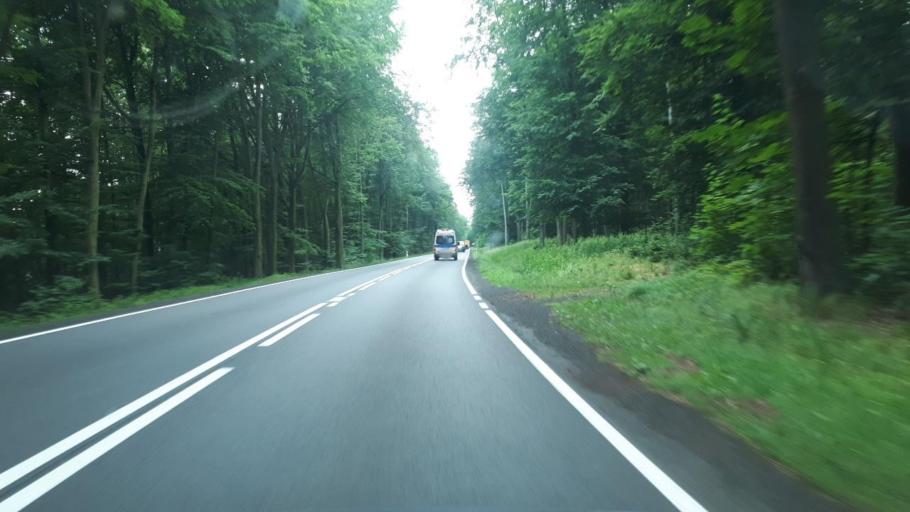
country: PL
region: Opole Voivodeship
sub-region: Powiat kluczborski
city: Kluczbork
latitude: 50.9616
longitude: 18.2890
